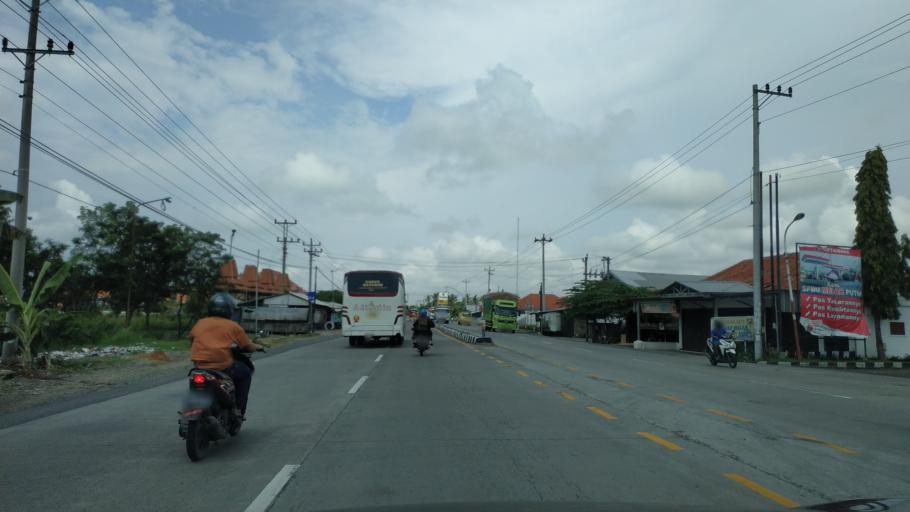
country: ID
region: Central Java
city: Tarub
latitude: -6.8712
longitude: 109.2384
